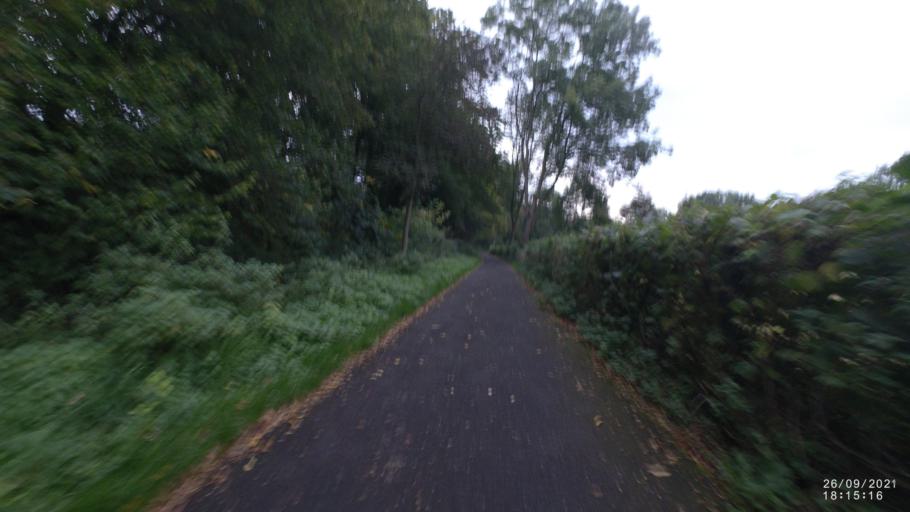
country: DE
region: North Rhine-Westphalia
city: Iserlohn
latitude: 51.4208
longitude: 7.6905
